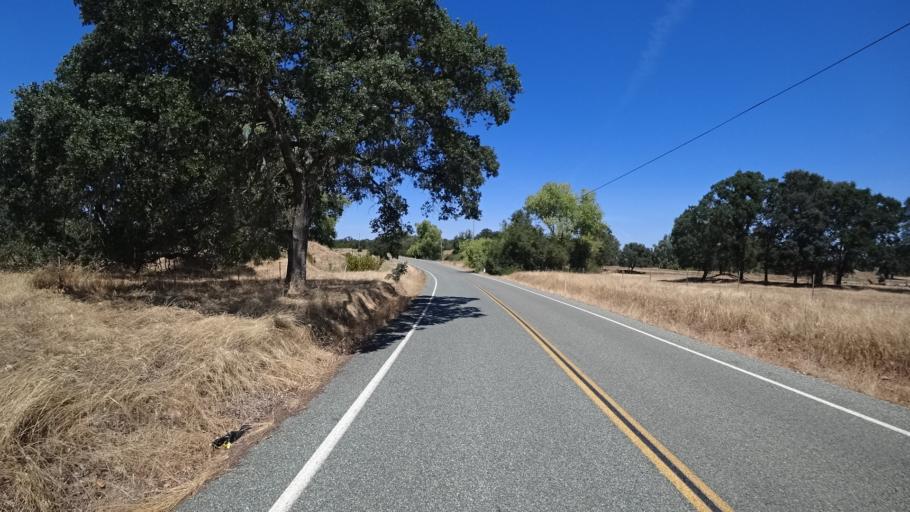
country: US
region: California
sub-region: Calaveras County
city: Rancho Calaveras
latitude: 38.2050
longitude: -120.9473
